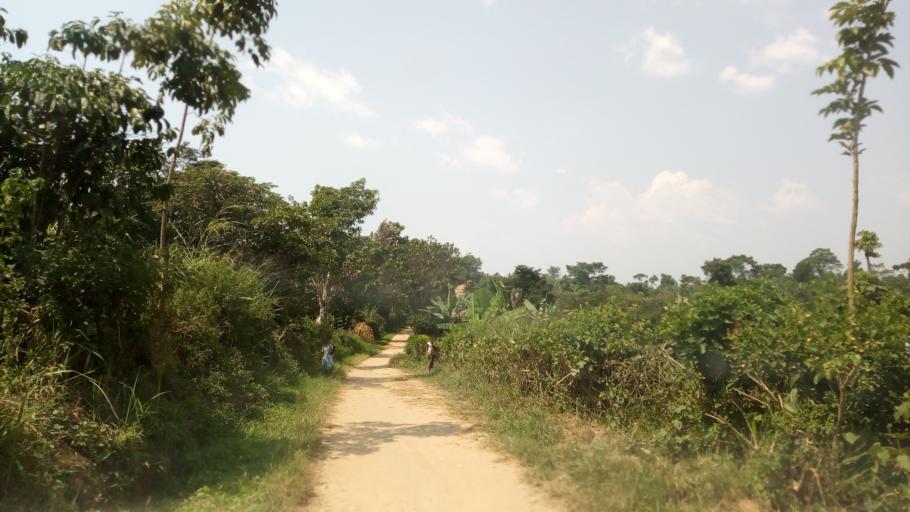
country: UG
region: Western Region
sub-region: Kanungu District
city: Ntungamo
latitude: -0.8059
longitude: 29.6466
